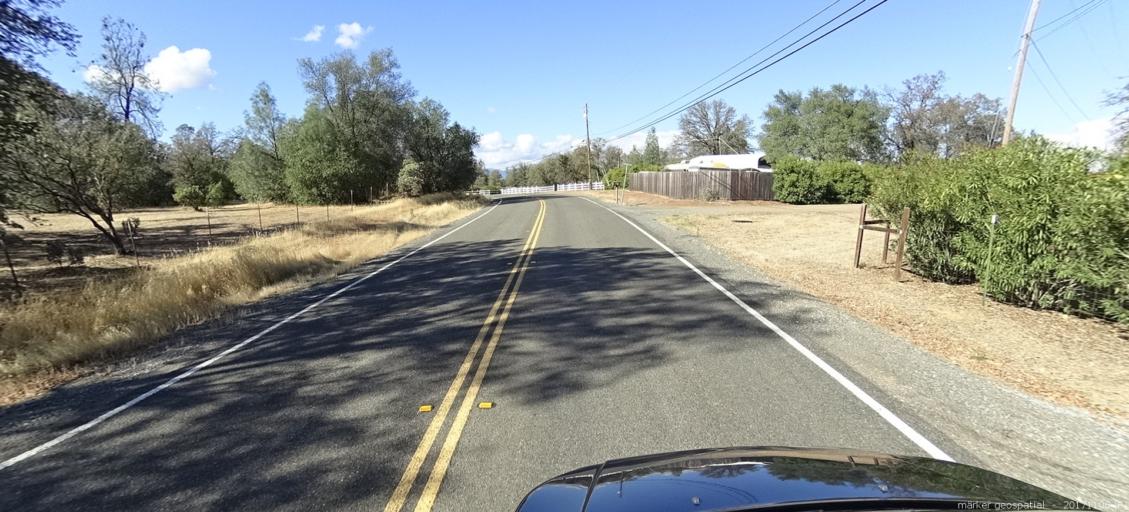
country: US
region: California
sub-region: Shasta County
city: Palo Cedro
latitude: 40.5931
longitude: -122.2818
